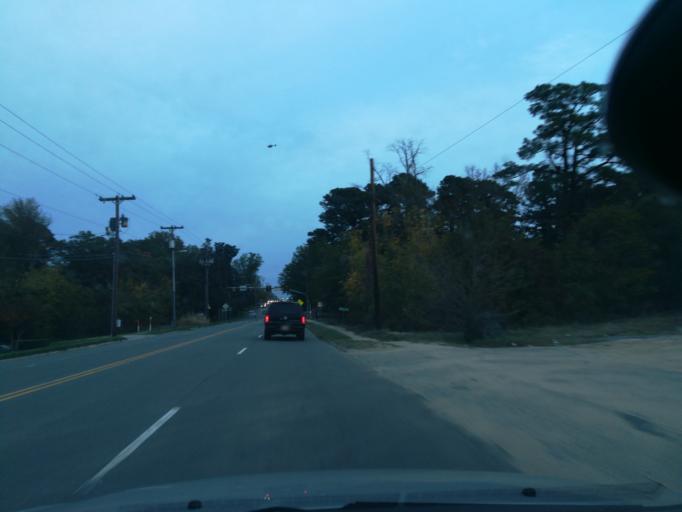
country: US
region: North Carolina
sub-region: Durham County
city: Durham
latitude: 36.0260
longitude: -78.9222
